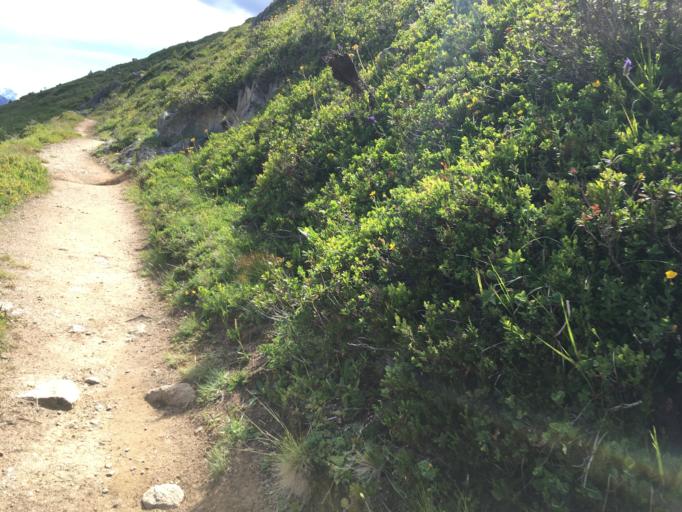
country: CH
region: Valais
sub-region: Goms District
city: Fiesch
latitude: 46.4310
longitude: 8.1193
